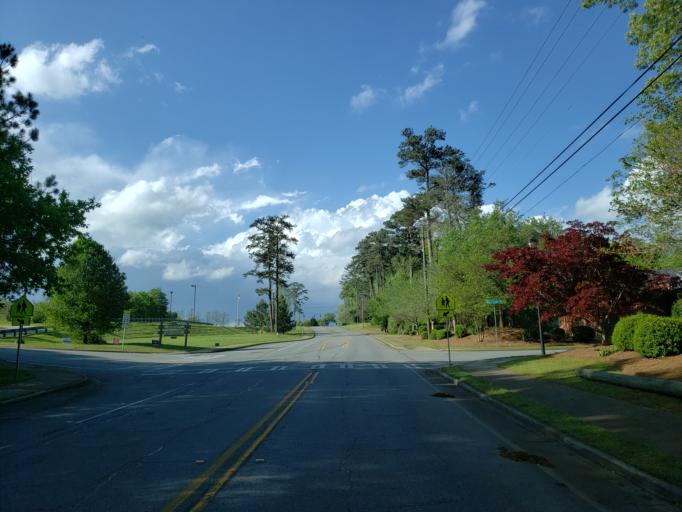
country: US
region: Georgia
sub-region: Fulton County
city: Roswell
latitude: 34.0564
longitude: -84.3346
